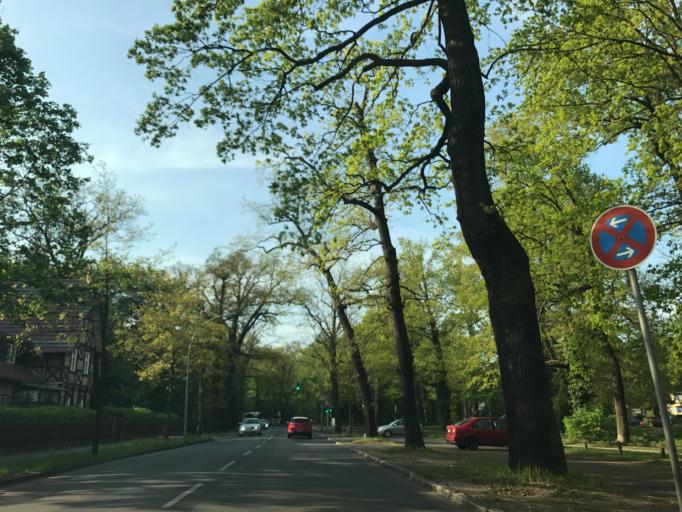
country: DE
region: Berlin
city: Spandau
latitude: 52.5612
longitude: 13.1973
